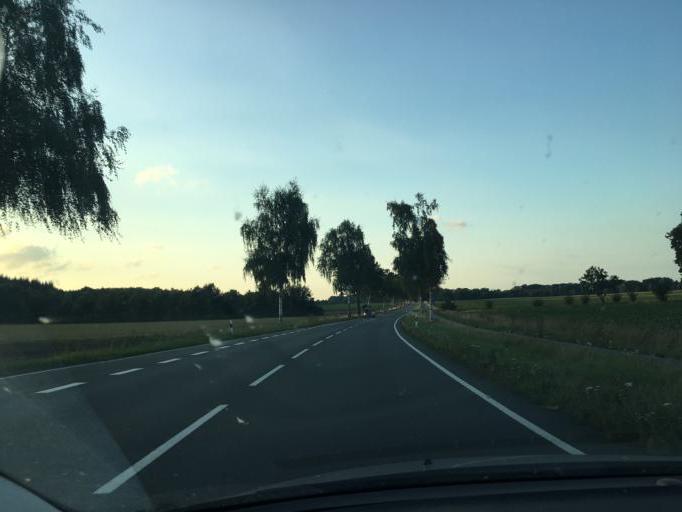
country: DE
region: Lower Saxony
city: Bergen
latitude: 52.8371
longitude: 9.9203
